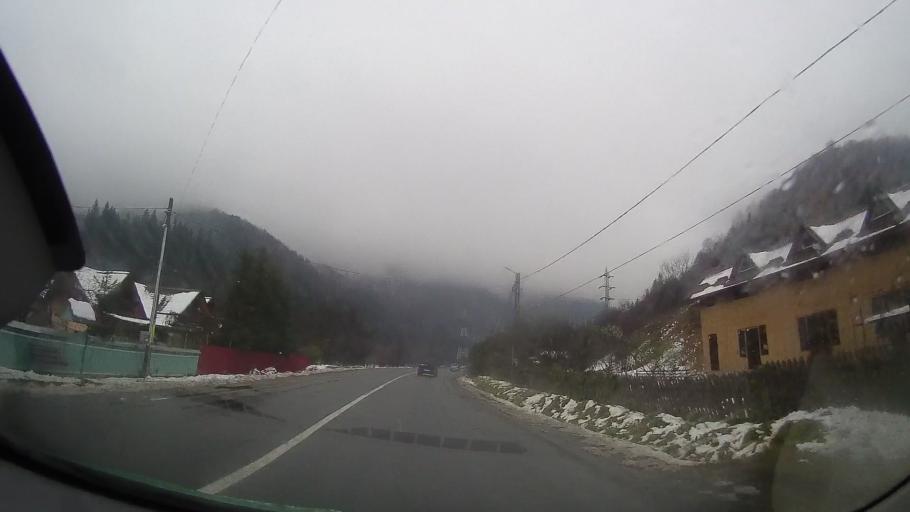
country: RO
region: Neamt
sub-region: Comuna Pangarati
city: Stejaru
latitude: 46.8943
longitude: 26.1694
